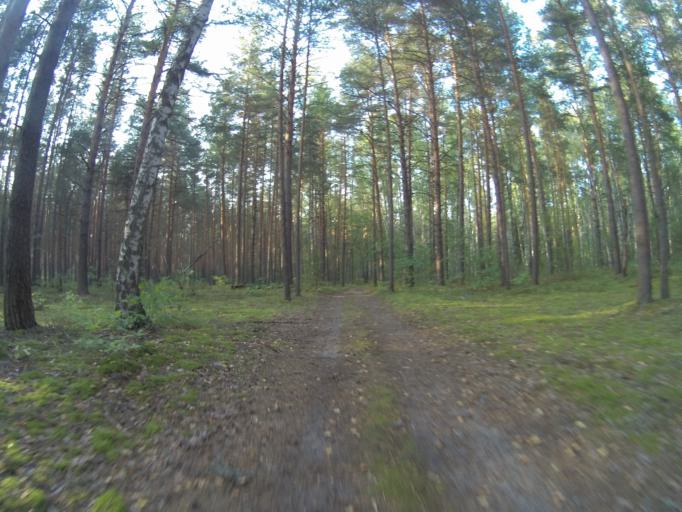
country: RU
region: Vladimir
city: Kommunar
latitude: 56.0743
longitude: 40.4342
